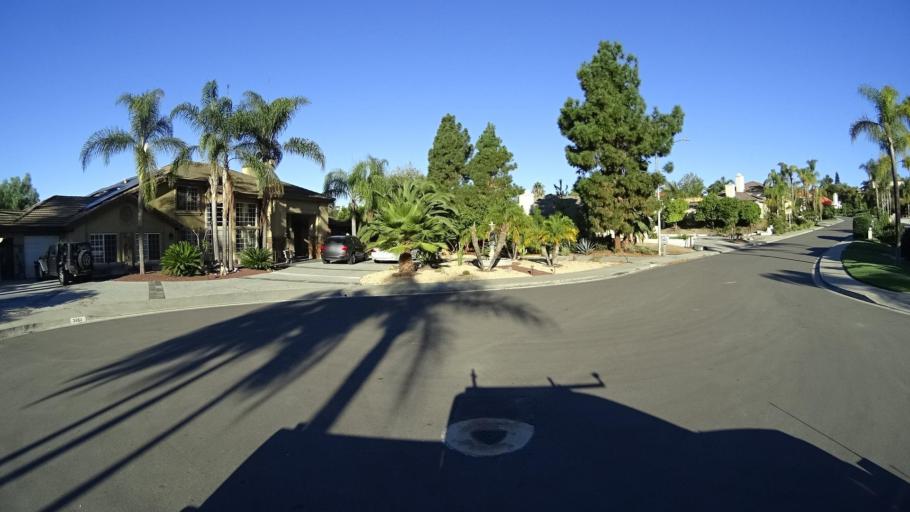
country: US
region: California
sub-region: San Diego County
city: Bonita
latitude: 32.6709
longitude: -117.0373
